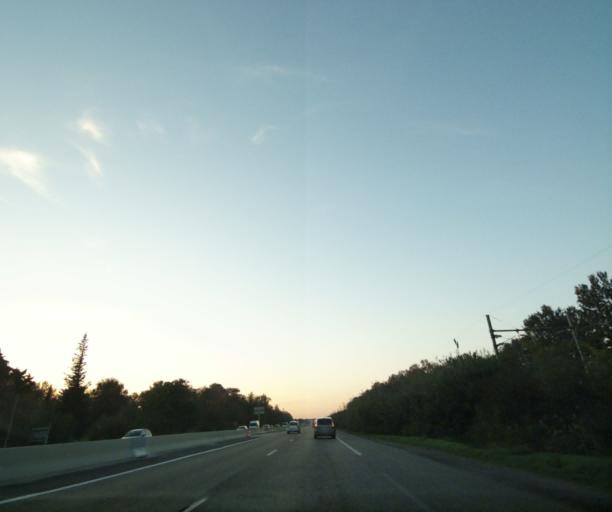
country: FR
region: Provence-Alpes-Cote d'Azur
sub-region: Departement des Bouches-du-Rhone
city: Fontvieille
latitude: 43.6405
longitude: 4.7201
